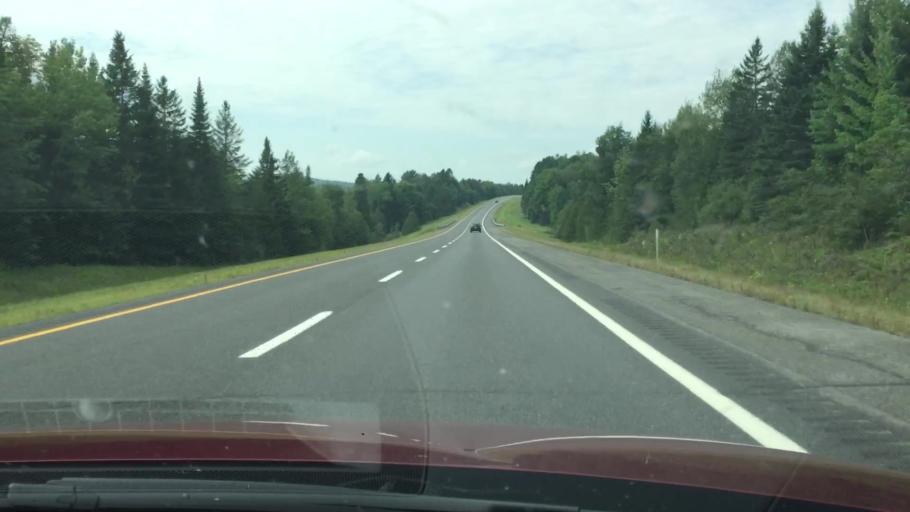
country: US
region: Maine
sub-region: Aroostook County
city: Hodgdon
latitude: 46.1407
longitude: -68.0082
